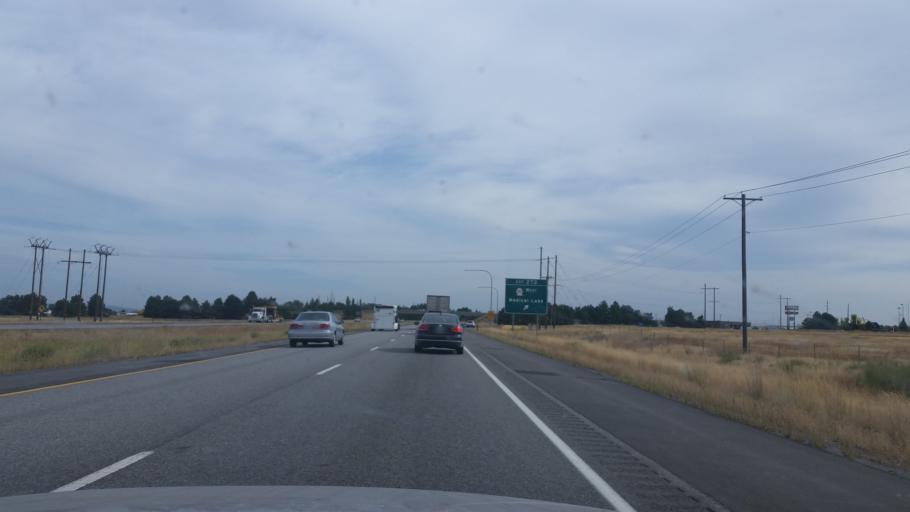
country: US
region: Washington
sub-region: Spokane County
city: Airway Heights
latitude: 47.5885
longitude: -117.5687
